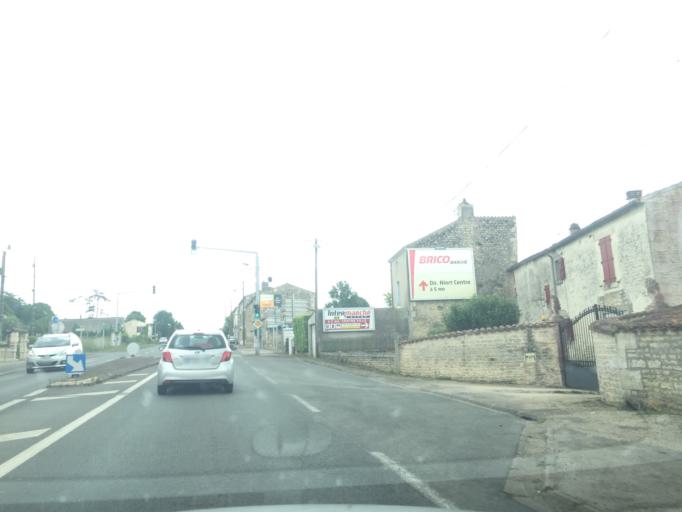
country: FR
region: Pays de la Loire
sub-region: Departement de la Vendee
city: Benet
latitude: 46.3735
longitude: -0.5852
